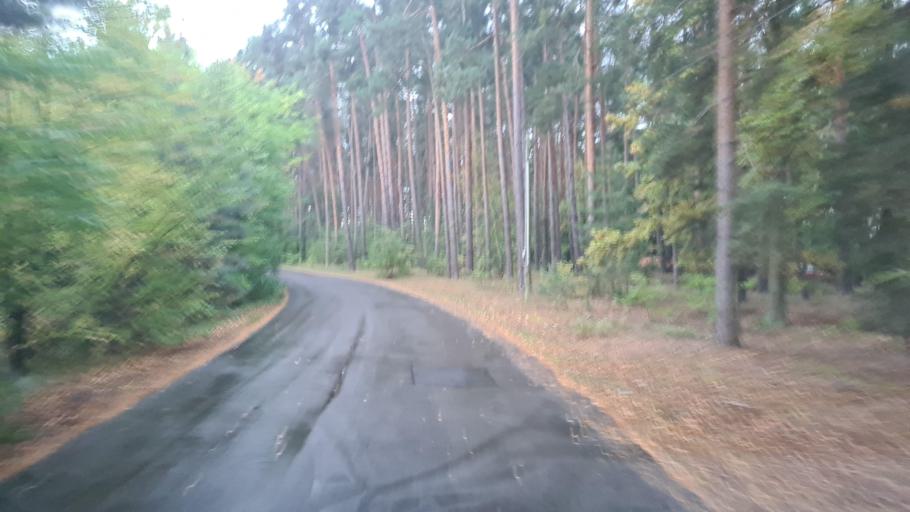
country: DE
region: Brandenburg
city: Munchehofe
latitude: 52.1324
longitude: 13.9415
